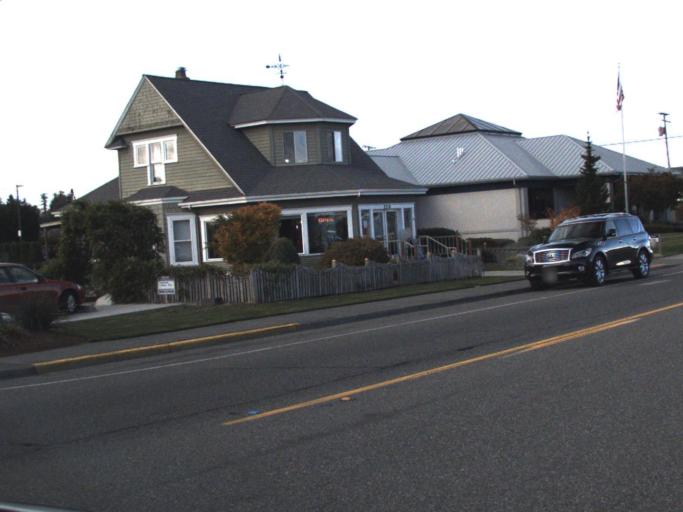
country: US
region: Washington
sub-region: Jefferson County
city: Port Hadlock-Irondale
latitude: 48.0101
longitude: -122.8305
